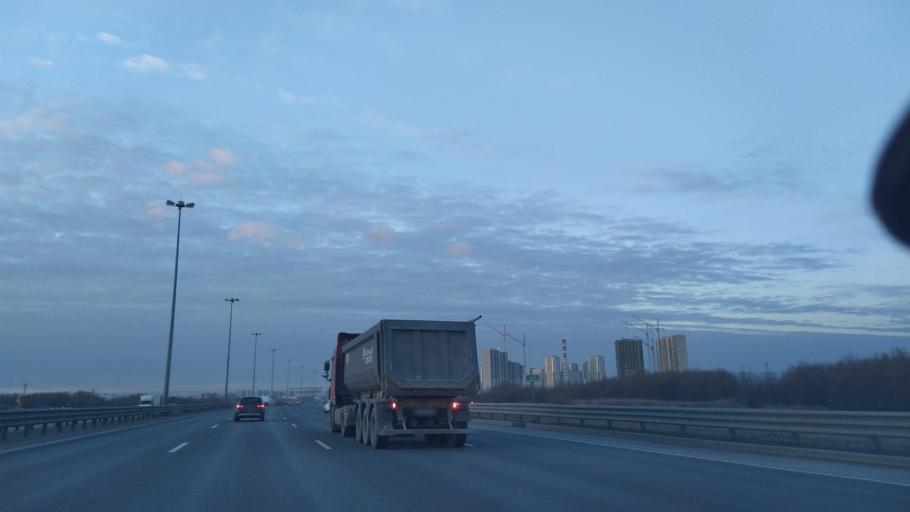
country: RU
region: St.-Petersburg
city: Krasnogvargeisky
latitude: 59.9954
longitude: 30.4785
